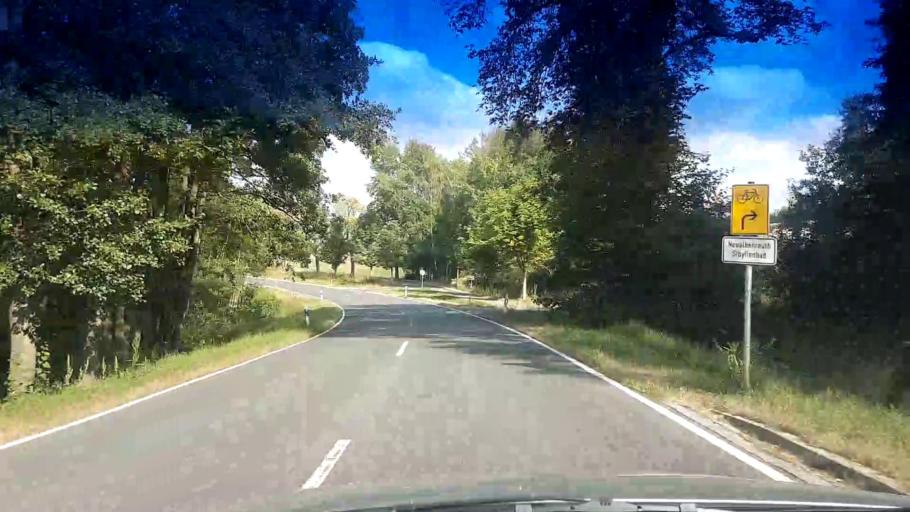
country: DE
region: Bavaria
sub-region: Upper Palatinate
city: Neualbenreuth
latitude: 49.9857
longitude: 12.4214
